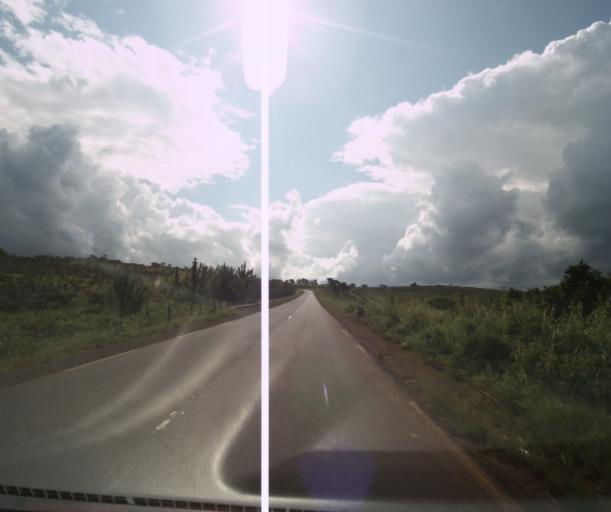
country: CM
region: West
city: Foumban
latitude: 5.7045
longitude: 10.8371
